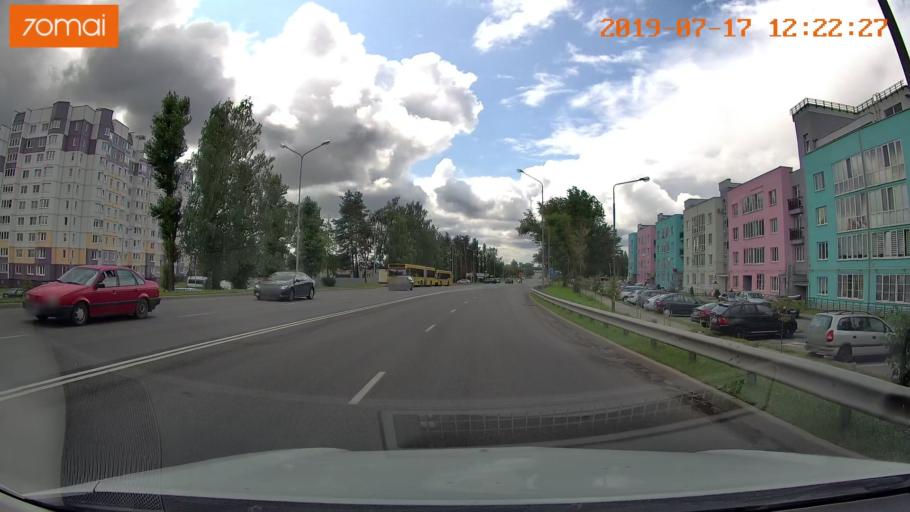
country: BY
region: Minsk
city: Borovlyany
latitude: 54.0013
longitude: 27.6775
